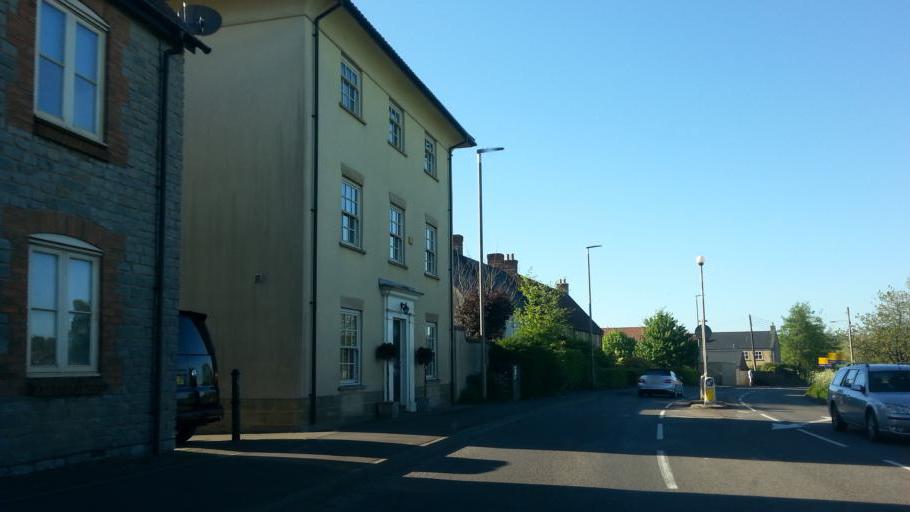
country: GB
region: England
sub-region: Somerset
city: Shepton Mallet
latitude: 51.1811
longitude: -2.5362
